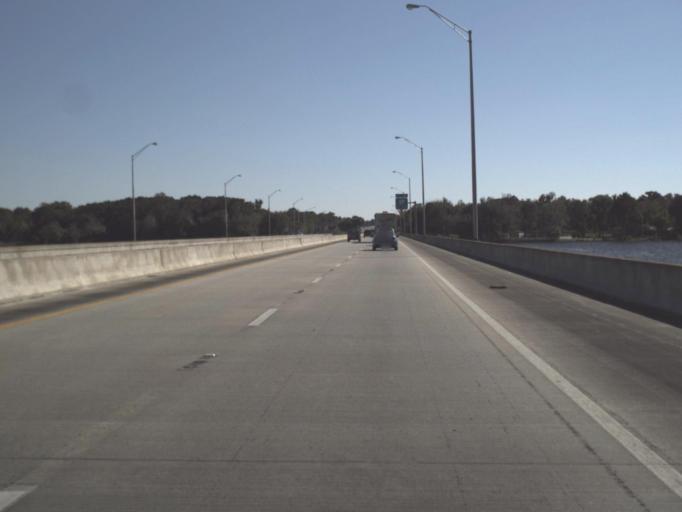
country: US
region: Florida
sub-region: Seminole County
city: Oviedo
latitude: 28.7044
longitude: -81.2351
